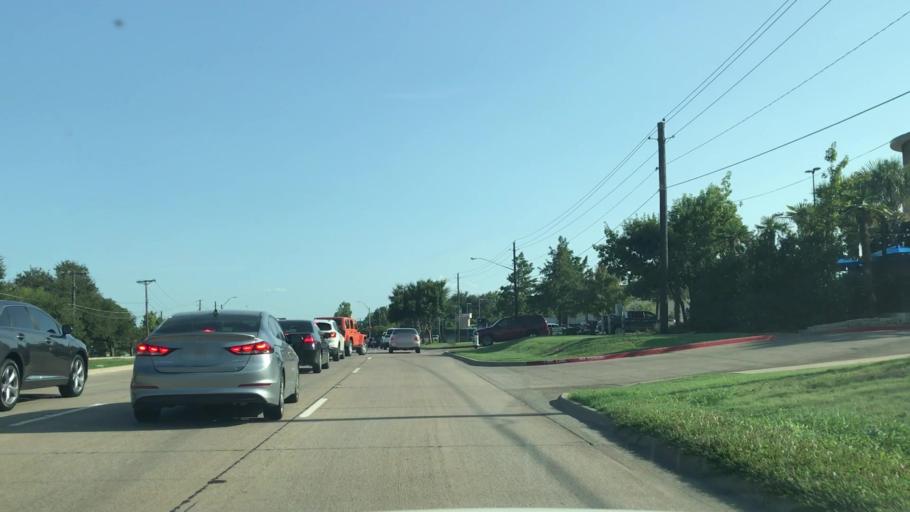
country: US
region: Texas
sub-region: Dallas County
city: Richardson
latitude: 32.8805
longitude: -96.7350
